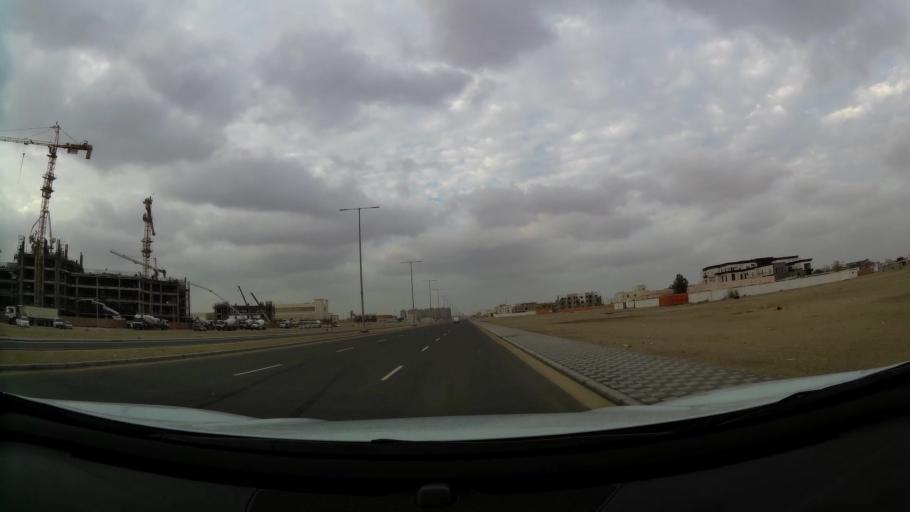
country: AE
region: Abu Dhabi
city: Abu Dhabi
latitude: 24.3536
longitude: 54.5405
